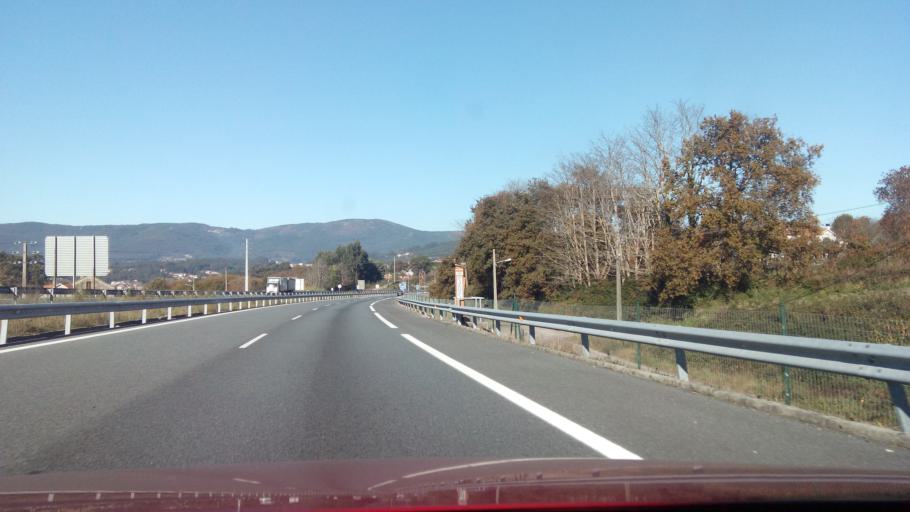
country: ES
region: Galicia
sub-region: Provincia de Pontevedra
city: Poio
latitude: 42.4066
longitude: -8.6523
